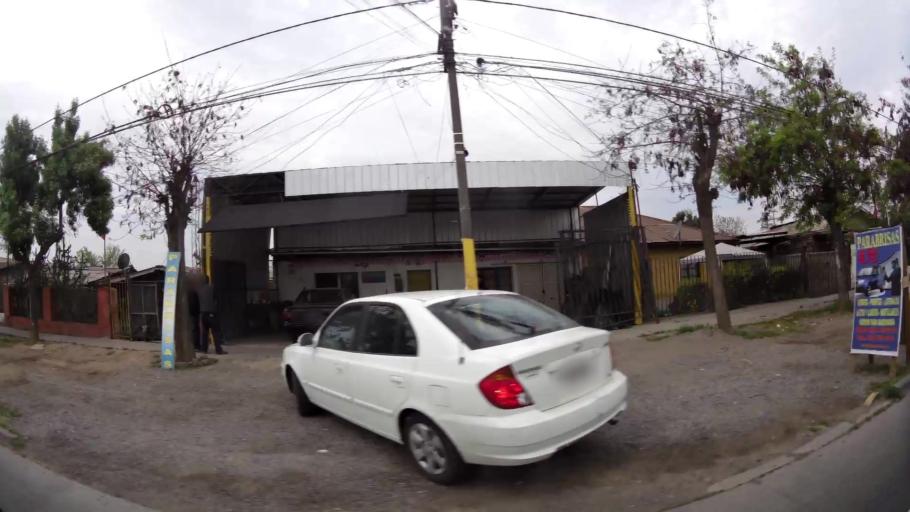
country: CL
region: Santiago Metropolitan
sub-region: Provincia de Santiago
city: Lo Prado
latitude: -33.5050
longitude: -70.7687
